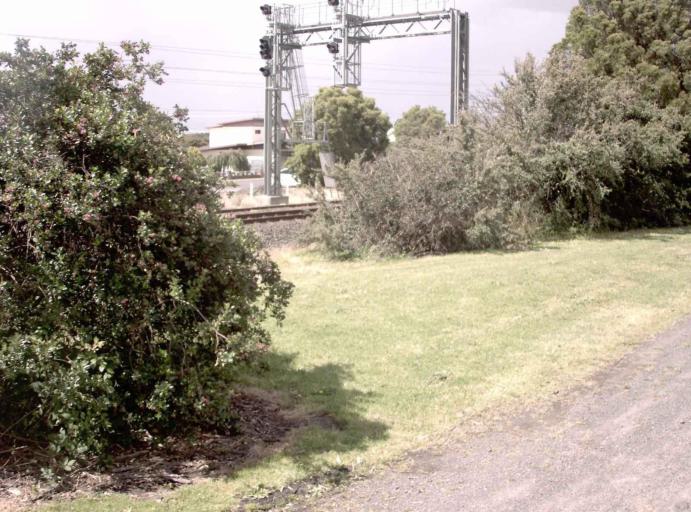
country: AU
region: Victoria
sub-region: Latrobe
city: Moe
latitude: -38.1811
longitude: 146.2471
